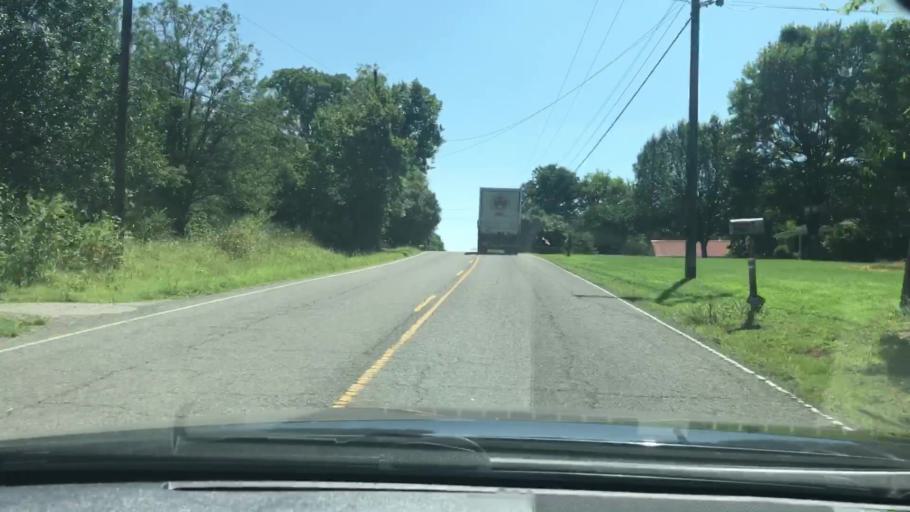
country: US
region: Tennessee
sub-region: Sumner County
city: Gallatin
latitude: 36.4007
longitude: -86.4863
